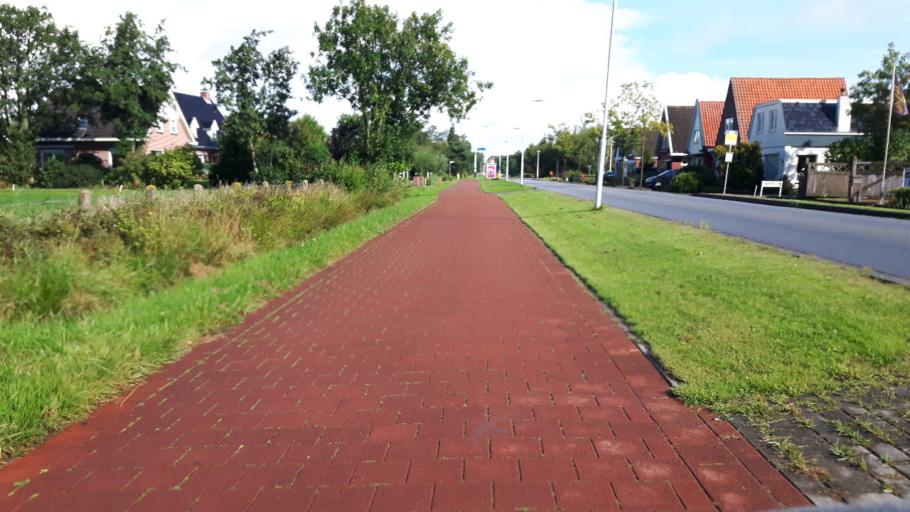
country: NL
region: Friesland
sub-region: Gemeente Smallingerland
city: Drachten
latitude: 53.0873
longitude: 6.0997
